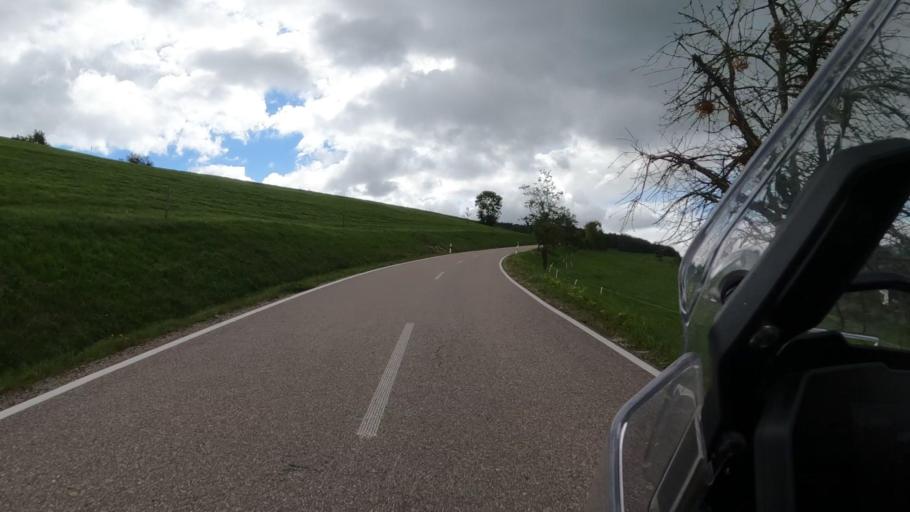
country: DE
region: Baden-Wuerttemberg
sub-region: Freiburg Region
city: Uhlingen-Birkendorf
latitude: 47.6997
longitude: 8.3470
